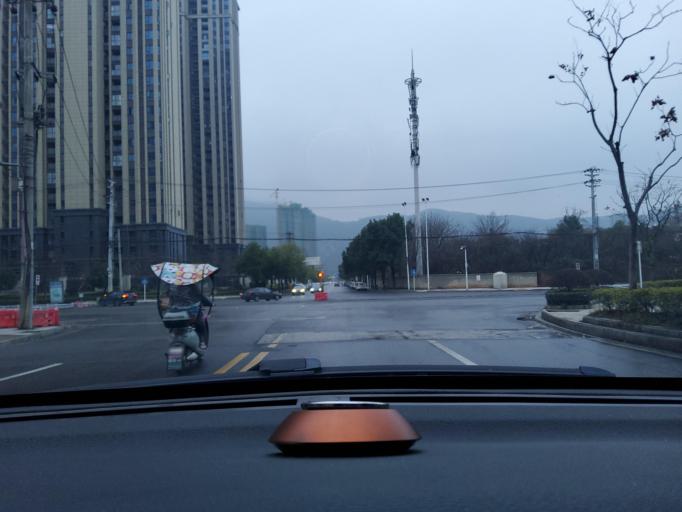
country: CN
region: Hubei
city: Tuanchengshan
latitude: 30.1956
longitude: 115.0094
